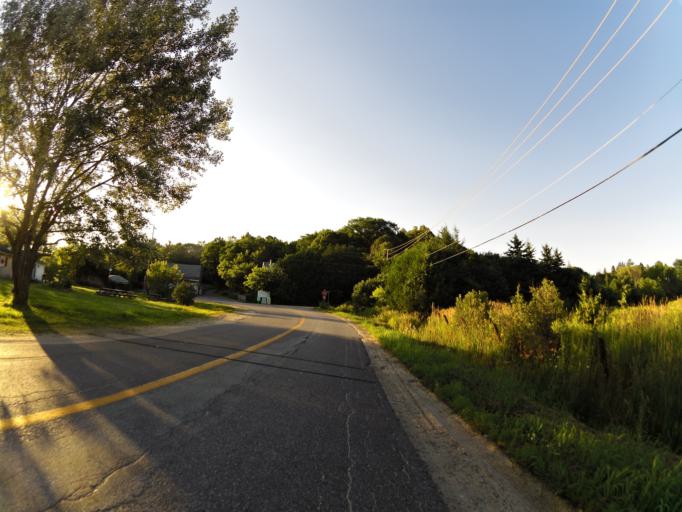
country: CA
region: Quebec
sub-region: Outaouais
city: Wakefield
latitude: 45.7081
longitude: -75.9602
